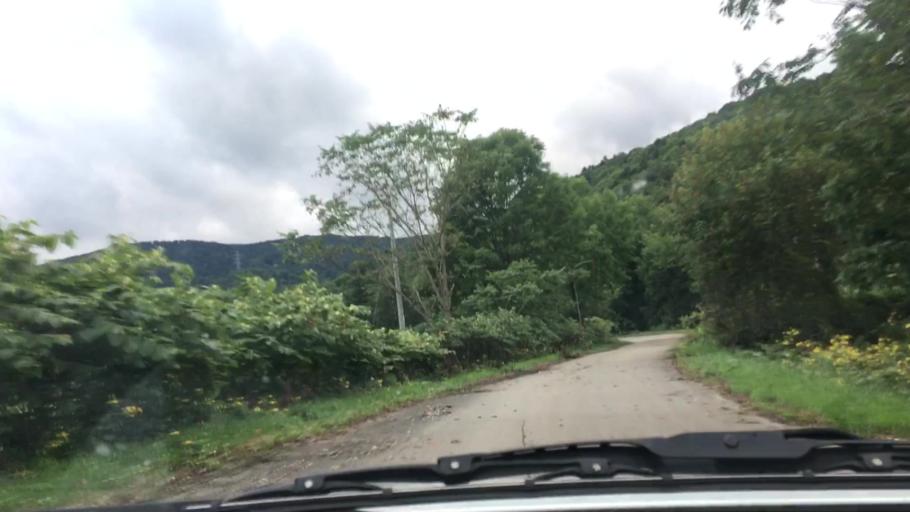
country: JP
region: Hokkaido
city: Shimo-furano
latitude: 43.0079
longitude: 142.4126
